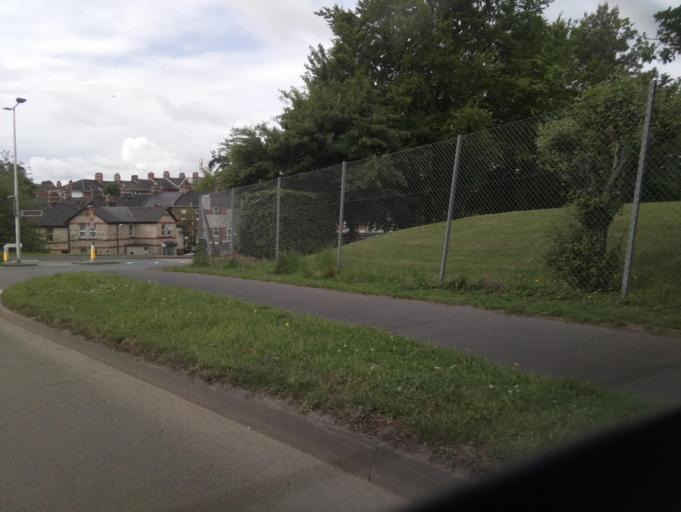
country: GB
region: England
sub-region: Devon
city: Newton Abbot
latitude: 50.5324
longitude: -3.6155
